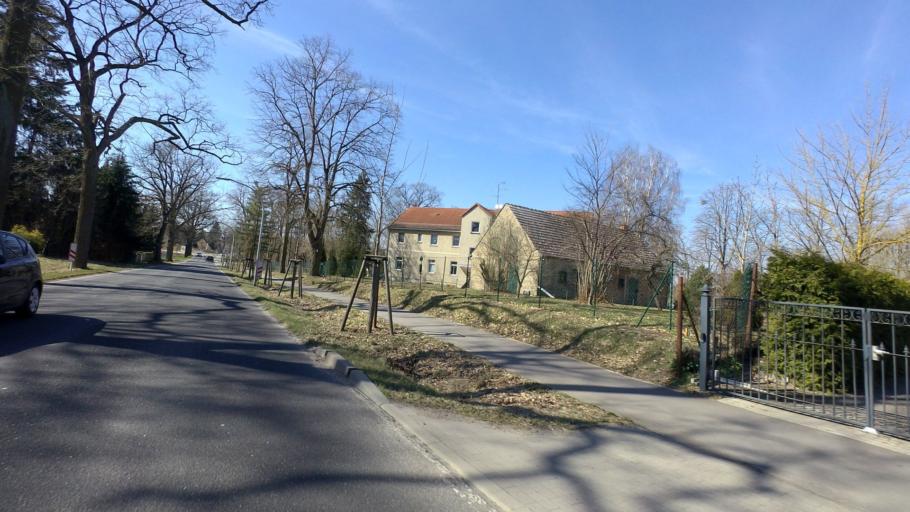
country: DE
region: Brandenburg
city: Waldsieversdorf
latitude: 52.5231
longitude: 14.0985
